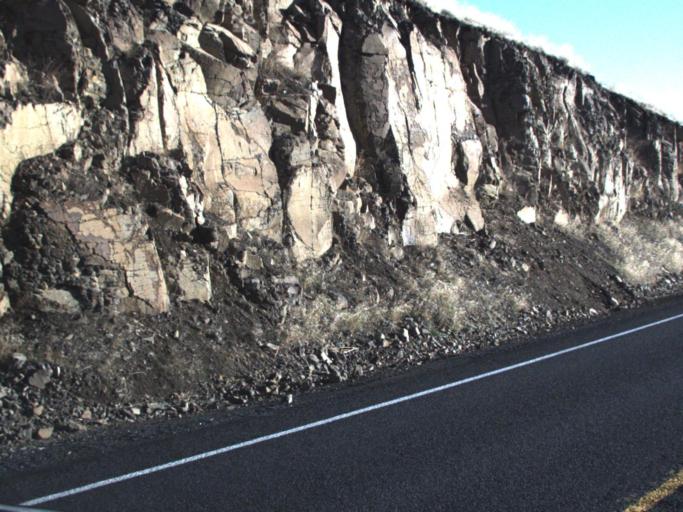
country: US
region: Washington
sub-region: Garfield County
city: Pomeroy
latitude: 46.5216
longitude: -117.8143
